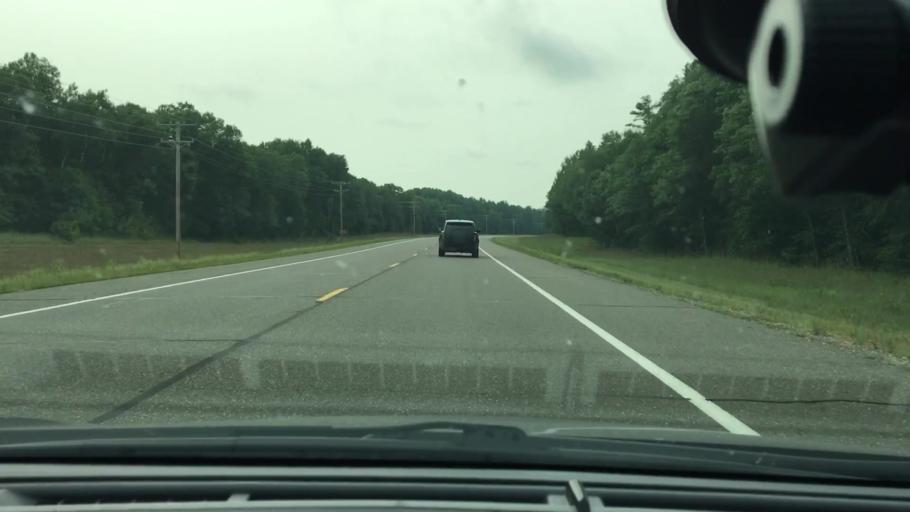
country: US
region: Minnesota
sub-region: Crow Wing County
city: Cross Lake
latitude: 46.6056
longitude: -94.1311
